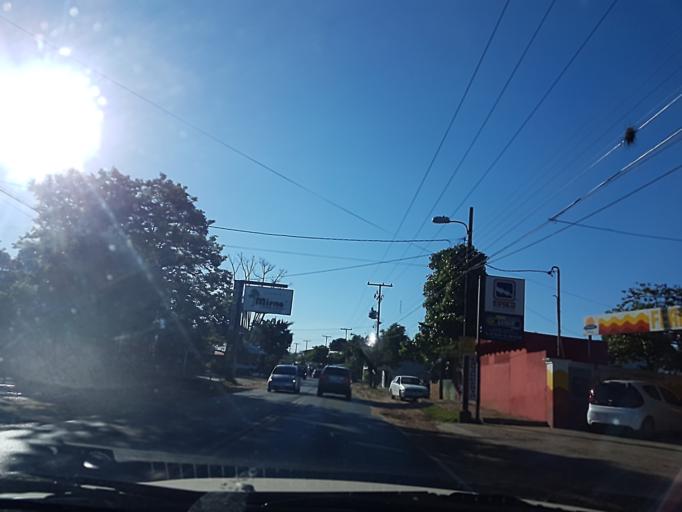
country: PY
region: Central
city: San Lorenzo
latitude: -25.2757
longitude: -57.4789
